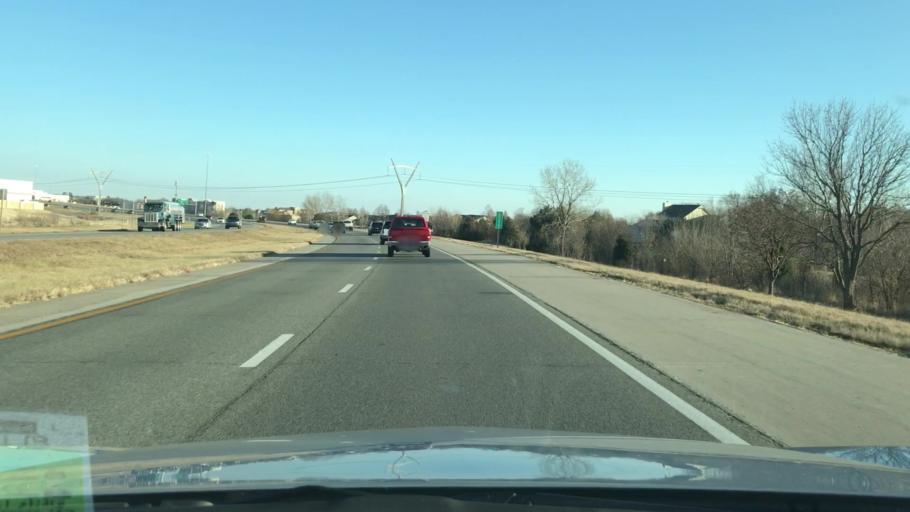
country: US
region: Kansas
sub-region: Sedgwick County
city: Bellaire
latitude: 37.7316
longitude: -97.2188
